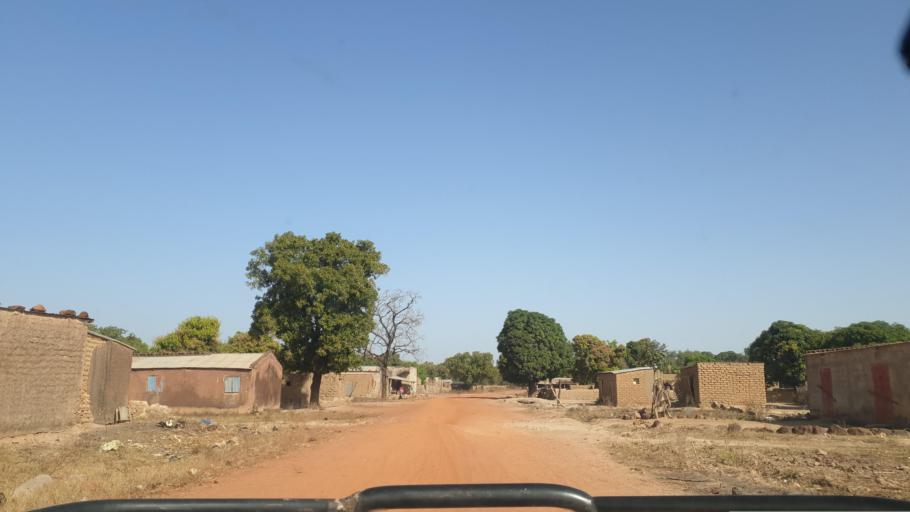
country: ML
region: Sikasso
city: Bougouni
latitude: 11.7680
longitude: -6.9023
